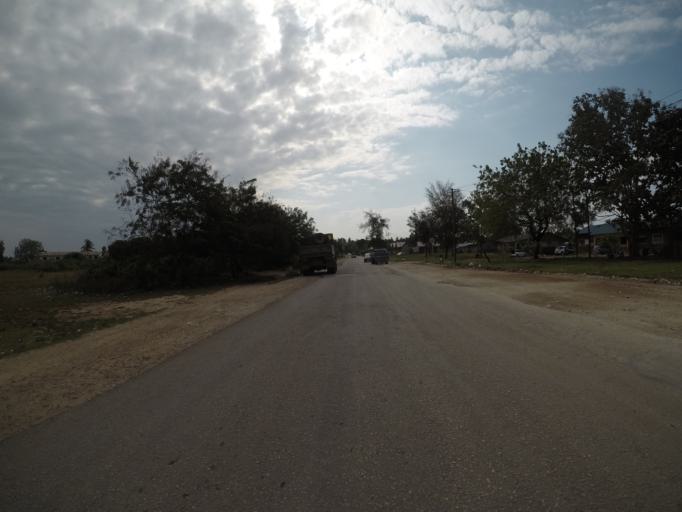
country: TZ
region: Zanzibar Central/South
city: Koani
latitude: -6.1959
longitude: 39.3048
